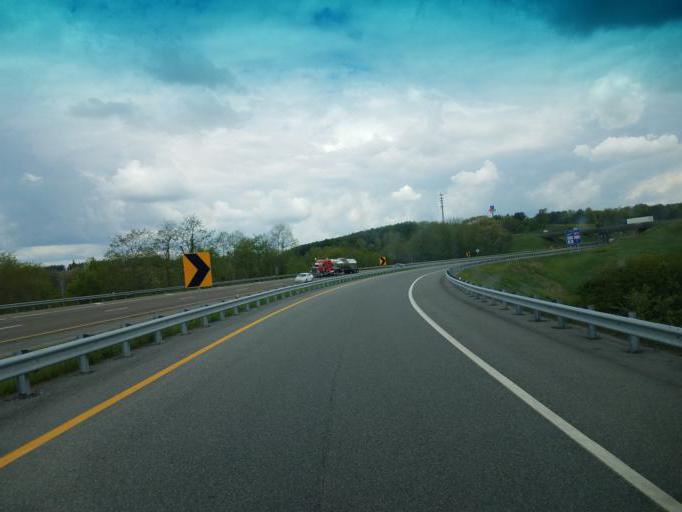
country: US
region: Virginia
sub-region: Wythe County
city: Wytheville
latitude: 36.9585
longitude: -81.0635
